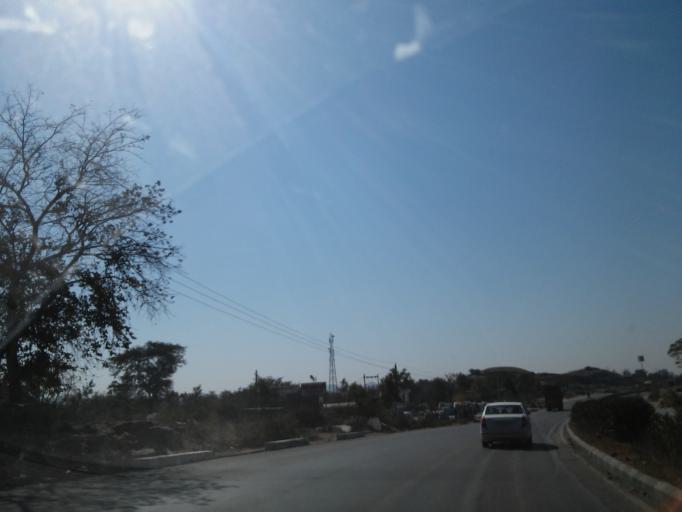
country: IN
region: Rajasthan
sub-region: Dungarpur
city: Dungarpur
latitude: 24.0839
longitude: 73.6871
